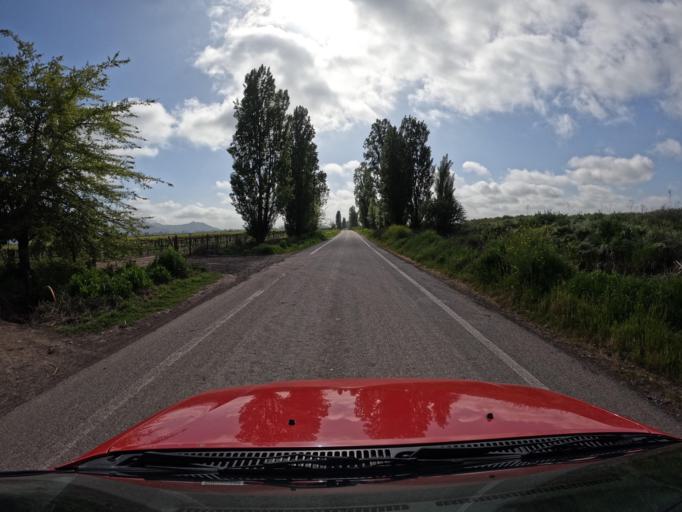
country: CL
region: Maule
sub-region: Provincia de Curico
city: Rauco
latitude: -34.8844
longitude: -71.2521
